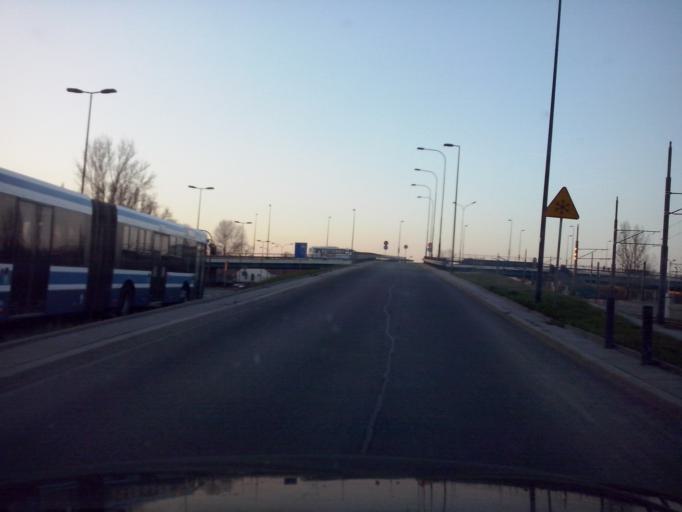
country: PL
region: Lesser Poland Voivodeship
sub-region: Krakow
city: Krakow
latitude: 50.0721
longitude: 19.9449
